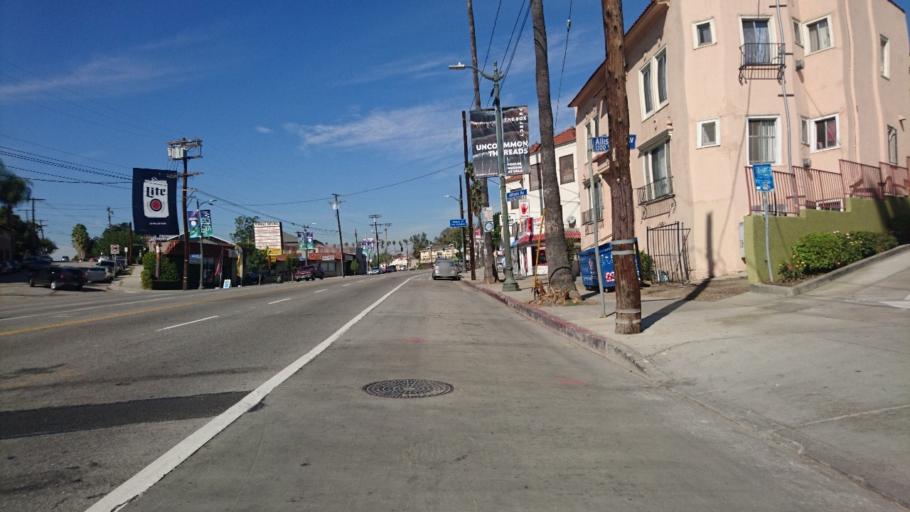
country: US
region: California
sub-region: Los Angeles County
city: Echo Park
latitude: 34.0728
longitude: -118.2511
